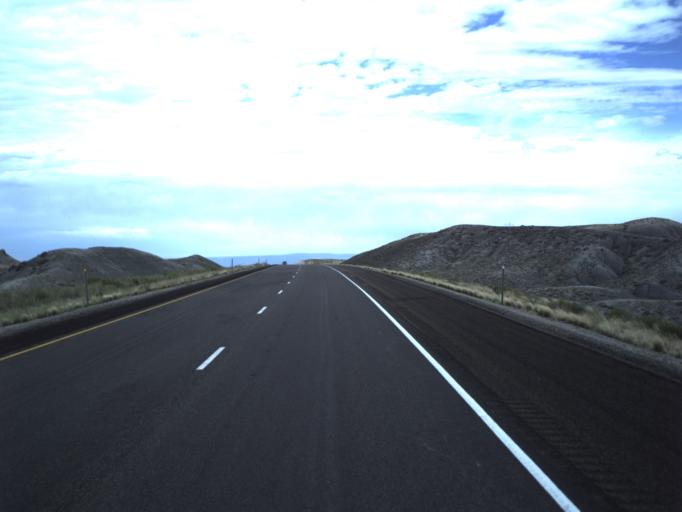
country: US
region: Utah
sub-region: Grand County
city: Moab
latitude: 38.9505
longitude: -109.6911
